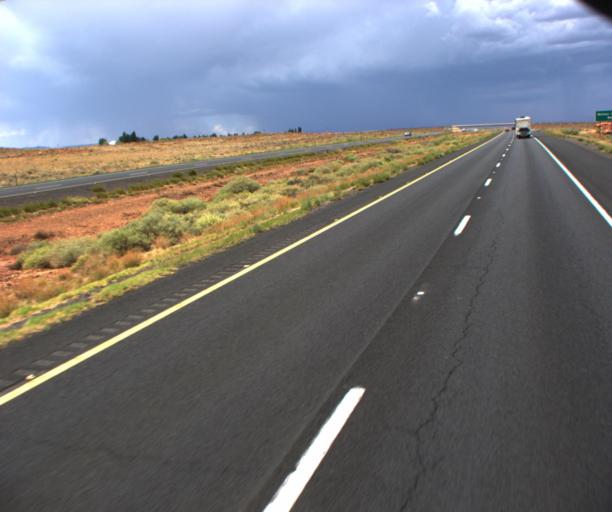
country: US
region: Arizona
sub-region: Coconino County
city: LeChee
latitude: 35.1094
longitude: -111.0227
